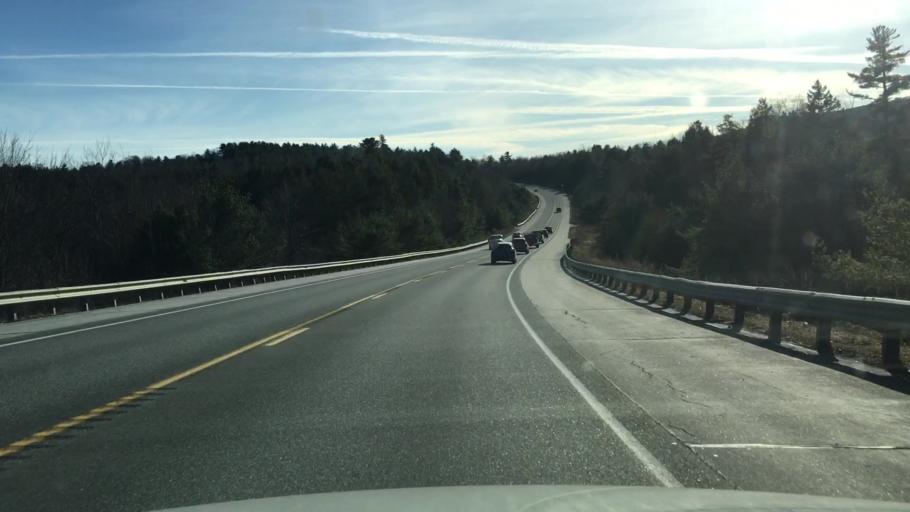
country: US
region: Maine
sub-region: Hancock County
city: Dedham
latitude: 44.6802
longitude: -68.5781
